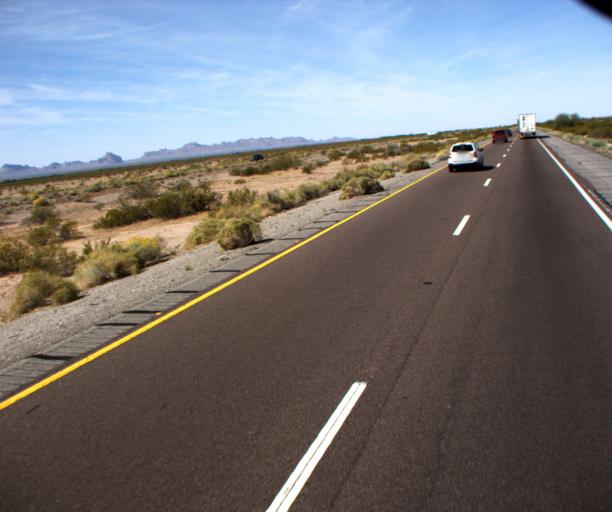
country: US
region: Arizona
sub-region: La Paz County
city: Salome
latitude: 33.5429
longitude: -113.1795
